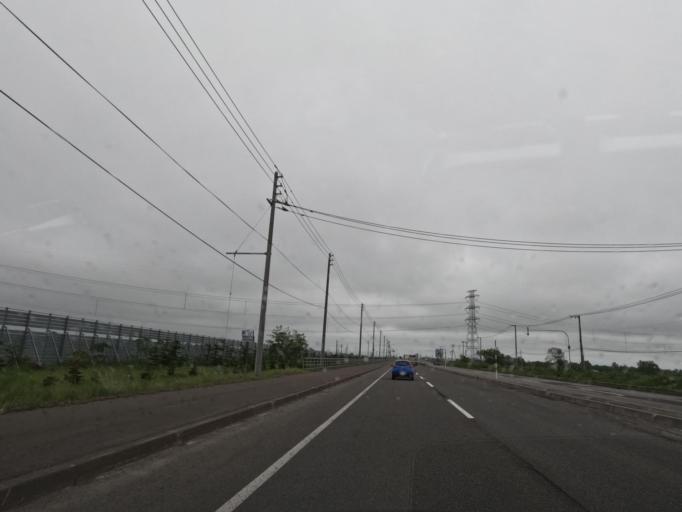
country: JP
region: Hokkaido
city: Tobetsu
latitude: 43.1595
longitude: 141.5192
